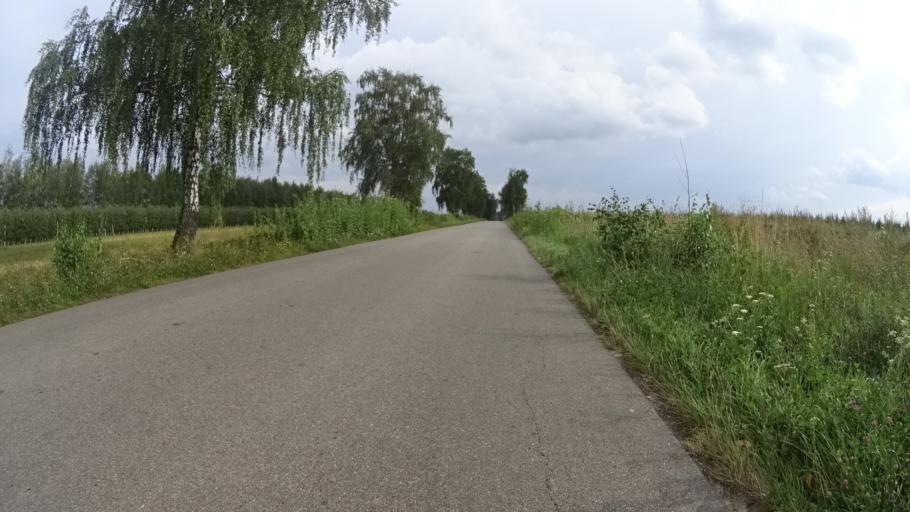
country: PL
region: Masovian Voivodeship
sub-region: Powiat grojecki
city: Goszczyn
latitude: 51.6955
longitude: 20.8564
